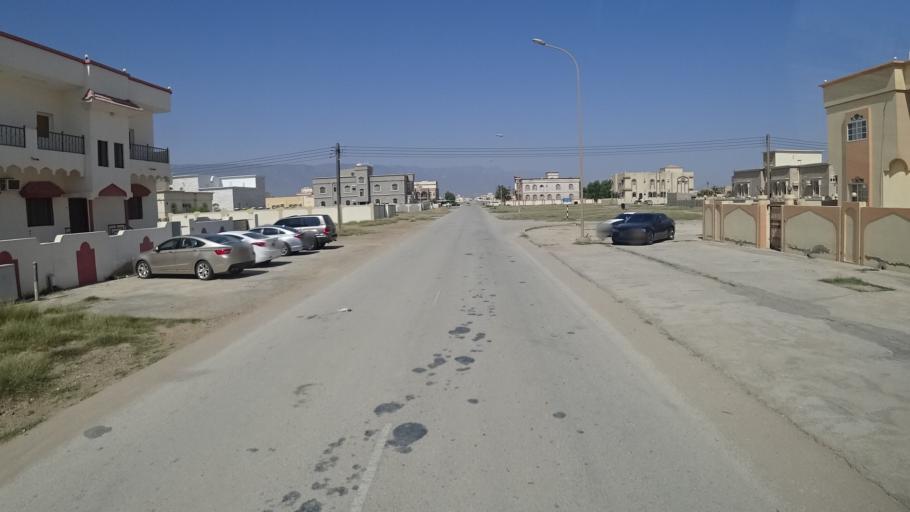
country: OM
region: Zufar
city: Salalah
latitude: 16.9836
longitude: 54.7071
